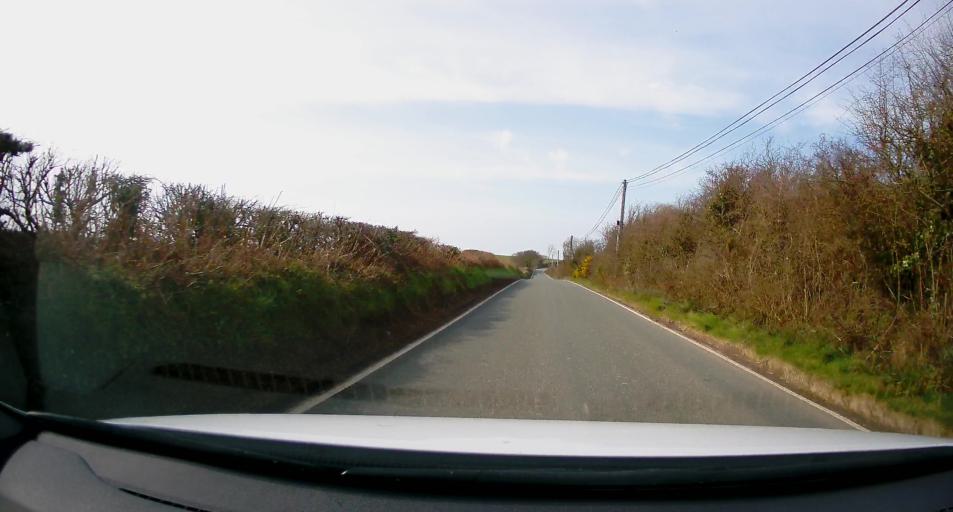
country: GB
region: Wales
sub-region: County of Ceredigion
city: Llanon
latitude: 52.2509
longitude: -4.2049
